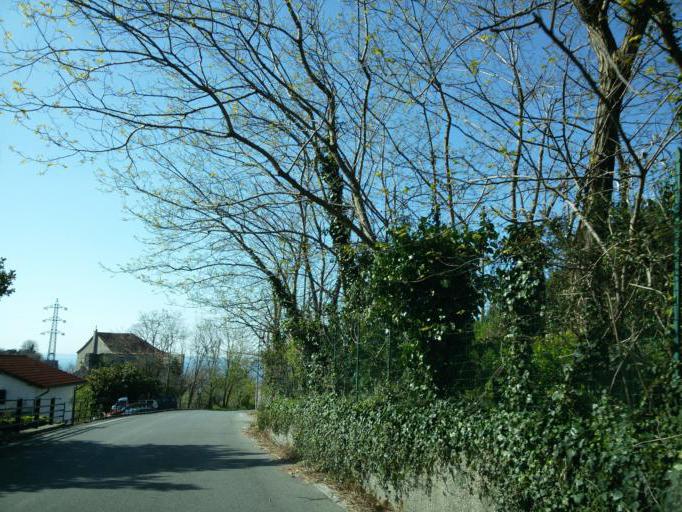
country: IT
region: Liguria
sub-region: Provincia di Genova
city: San Teodoro
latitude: 44.4231
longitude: 8.9039
